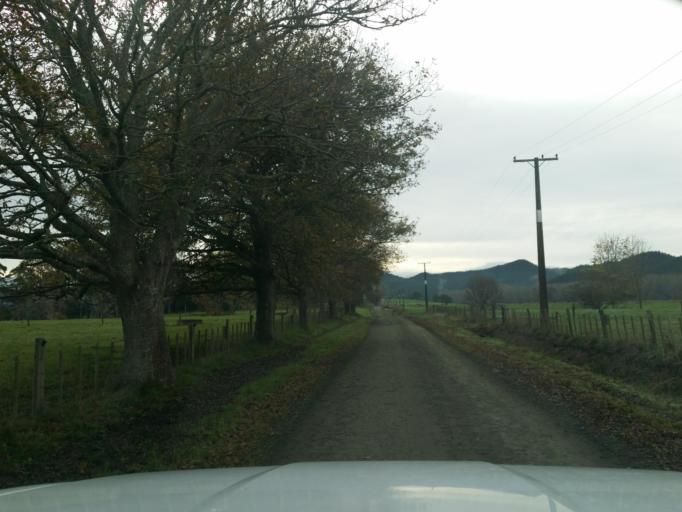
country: NZ
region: Northland
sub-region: Whangarei
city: Maungatapere
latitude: -35.7998
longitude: 174.0521
